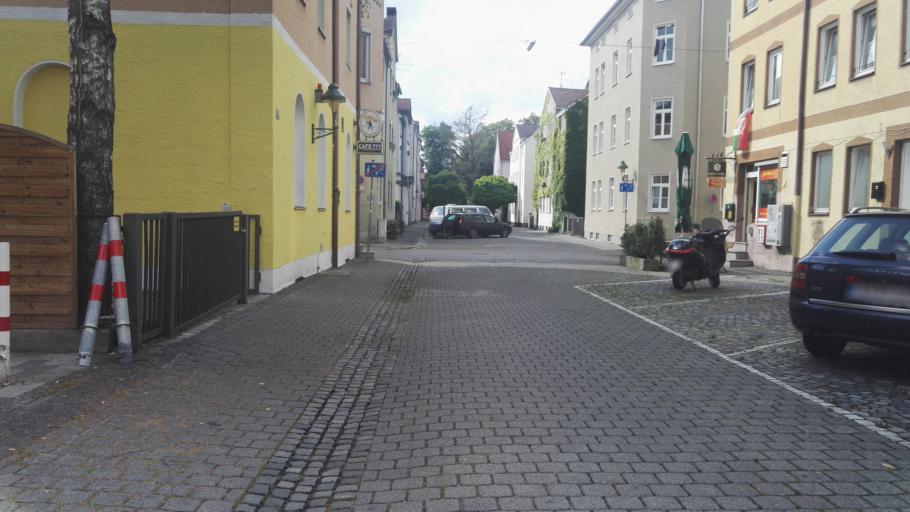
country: DE
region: Bavaria
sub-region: Swabia
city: Augsburg
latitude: 48.3773
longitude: 10.8784
